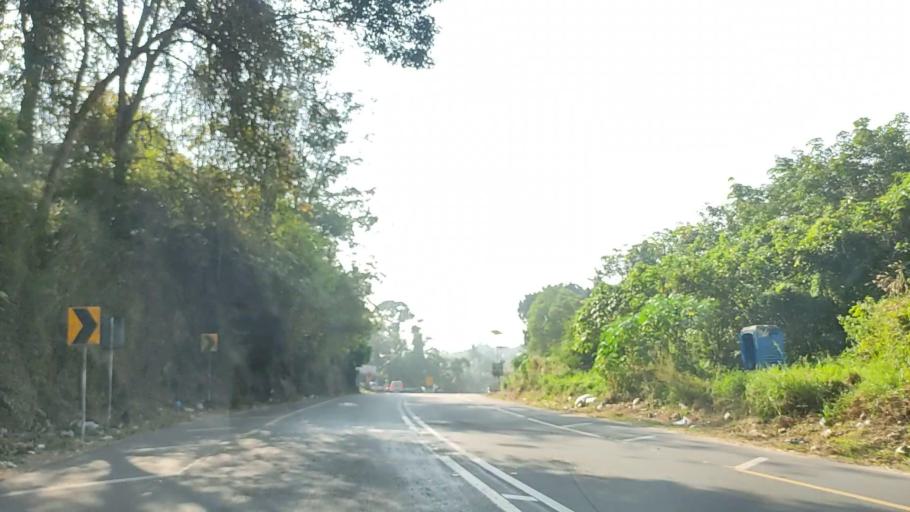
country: IN
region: Kerala
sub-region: Kollam
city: Punalur
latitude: 8.8908
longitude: 76.8668
